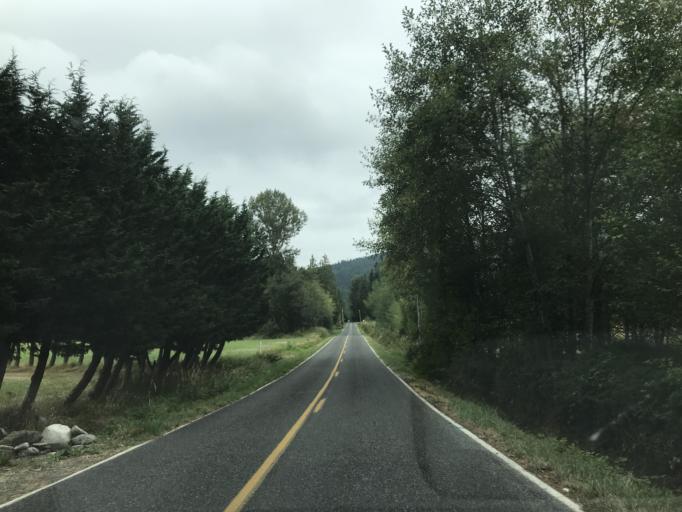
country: US
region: Washington
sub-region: Whatcom County
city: Sudden Valley
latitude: 48.7749
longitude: -122.3367
